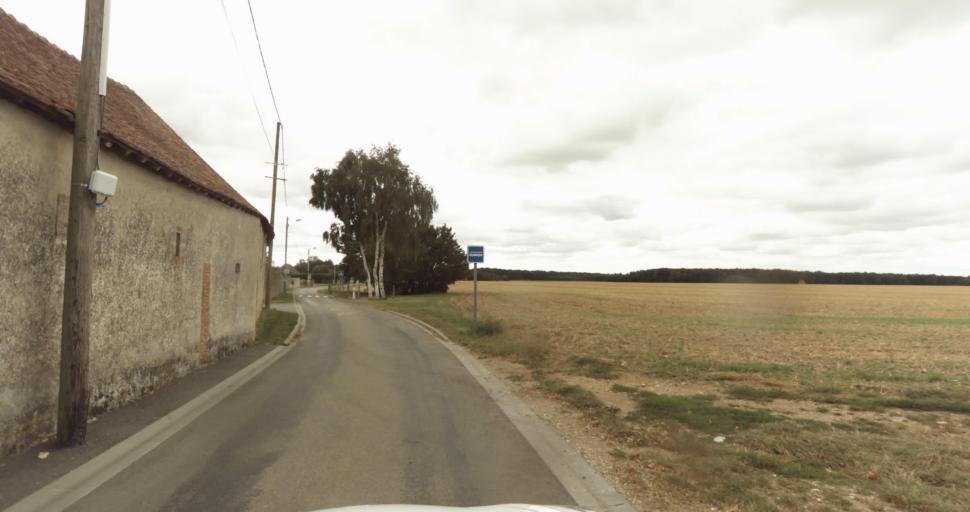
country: FR
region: Haute-Normandie
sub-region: Departement de l'Eure
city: La Madeleine-de-Nonancourt
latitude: 48.8215
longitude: 1.2041
